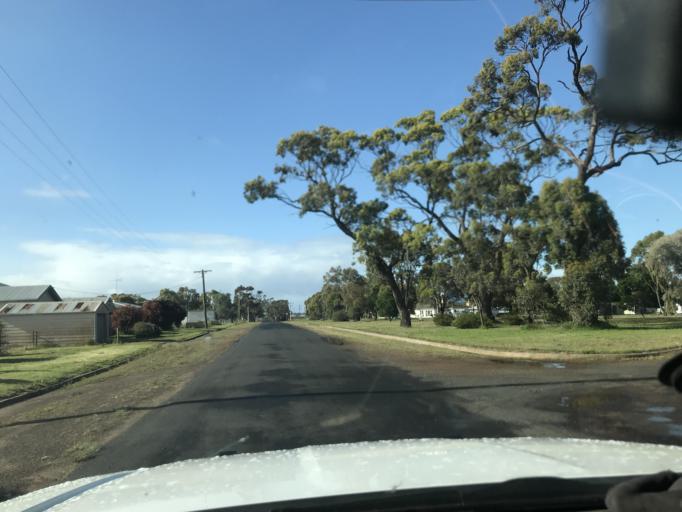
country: AU
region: Victoria
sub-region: Horsham
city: Horsham
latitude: -36.7199
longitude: 141.4768
